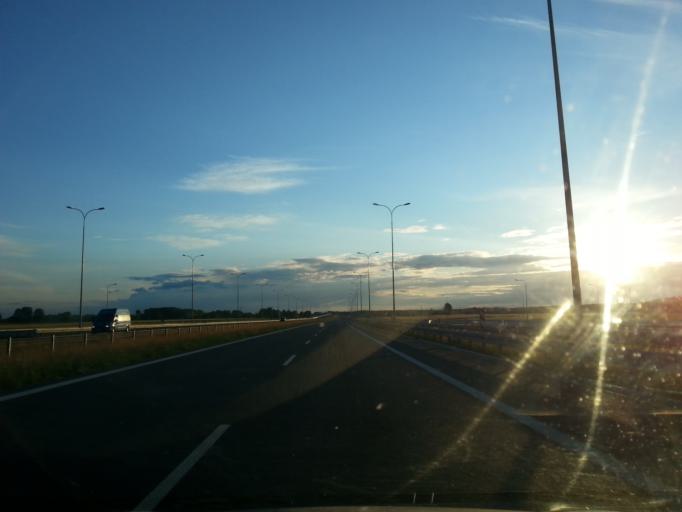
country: PL
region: Greater Poland Voivodeship
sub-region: Powiat kepinski
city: Kepno
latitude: 51.3158
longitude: 18.0081
